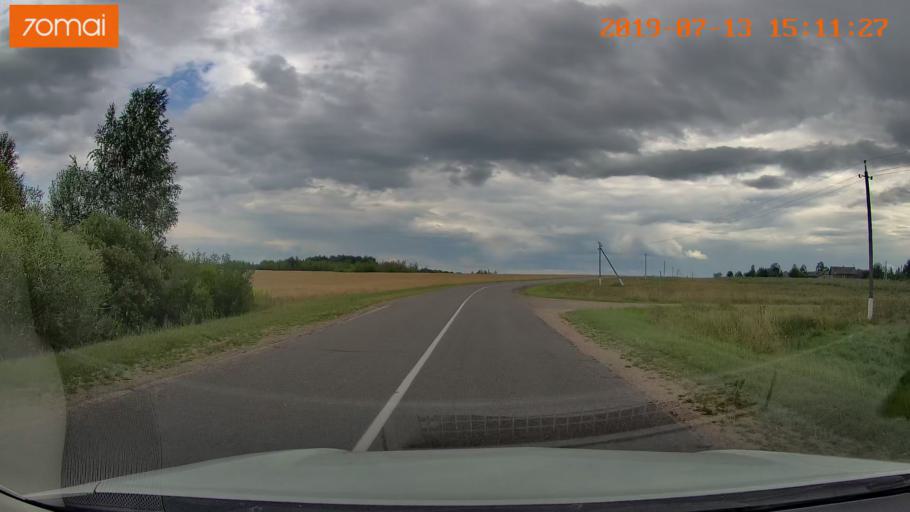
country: BY
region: Mogilev
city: Hlusha
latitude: 53.1610
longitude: 28.7857
